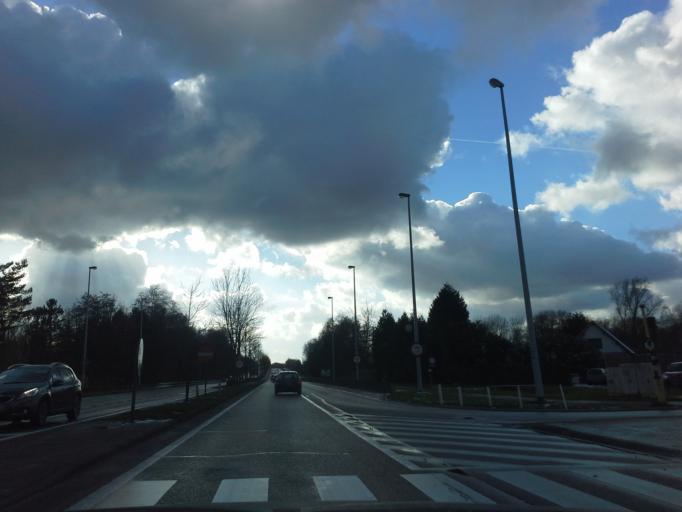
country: BE
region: Flanders
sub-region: Provincie Antwerpen
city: Mol
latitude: 51.1995
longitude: 5.1439
